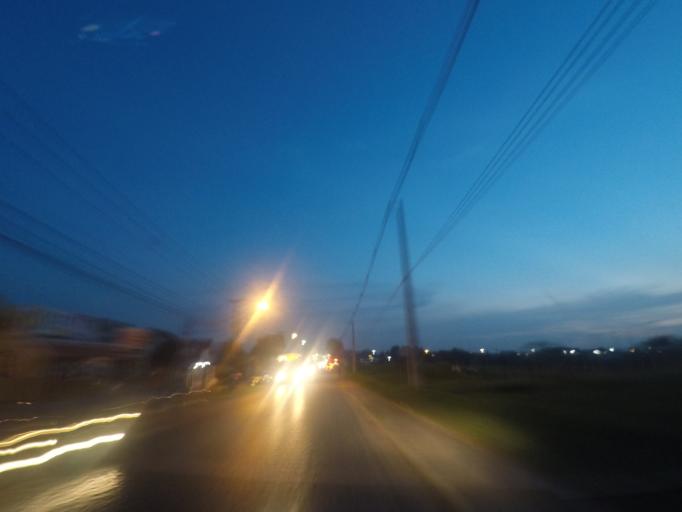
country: BR
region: Parana
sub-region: Pinhais
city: Pinhais
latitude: -25.4865
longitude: -49.1544
